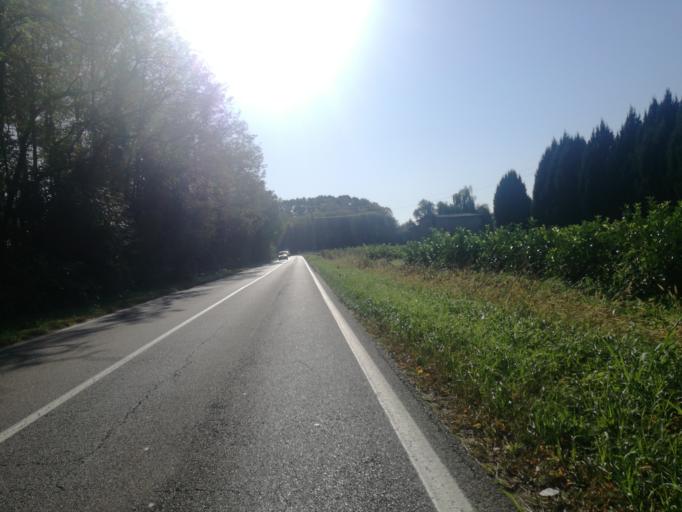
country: IT
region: Lombardy
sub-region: Provincia di Monza e Brianza
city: Cornate d'Adda
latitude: 45.6339
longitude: 9.4903
